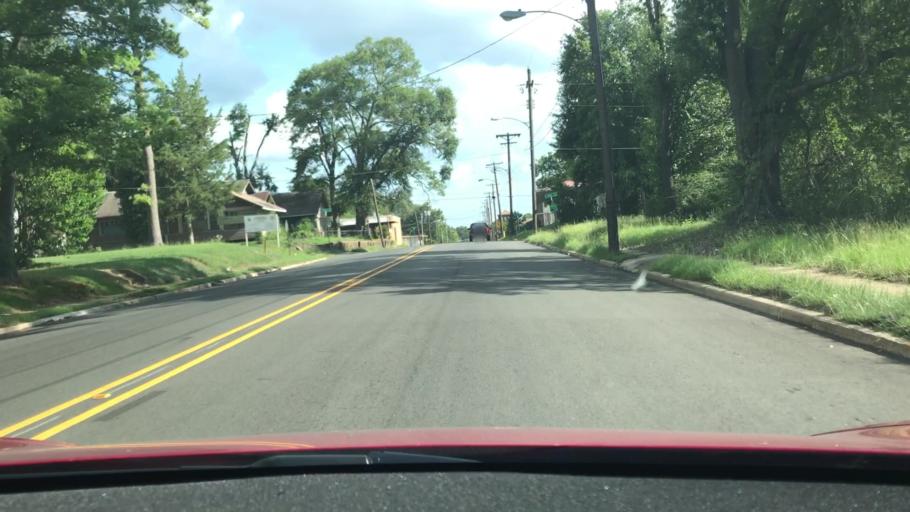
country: US
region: Louisiana
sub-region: Bossier Parish
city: Bossier City
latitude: 32.4463
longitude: -93.7545
